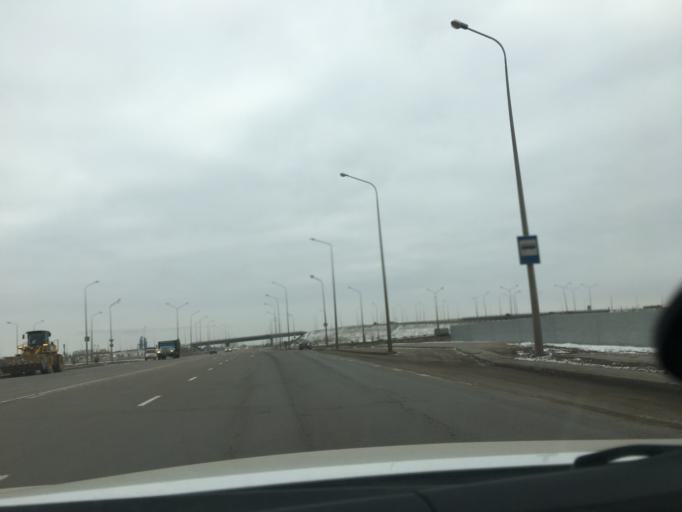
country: KZ
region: Astana Qalasy
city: Astana
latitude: 51.1564
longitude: 71.5292
